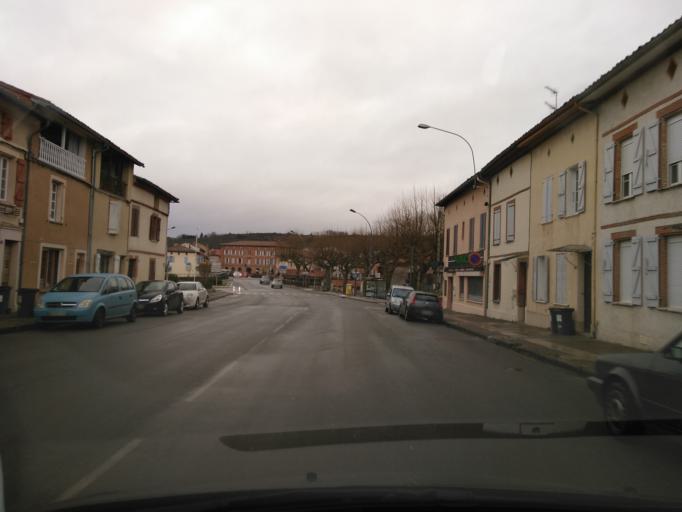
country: FR
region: Midi-Pyrenees
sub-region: Departement de la Haute-Garonne
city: Montesquieu-Volvestre
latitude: 43.2048
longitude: 1.2283
